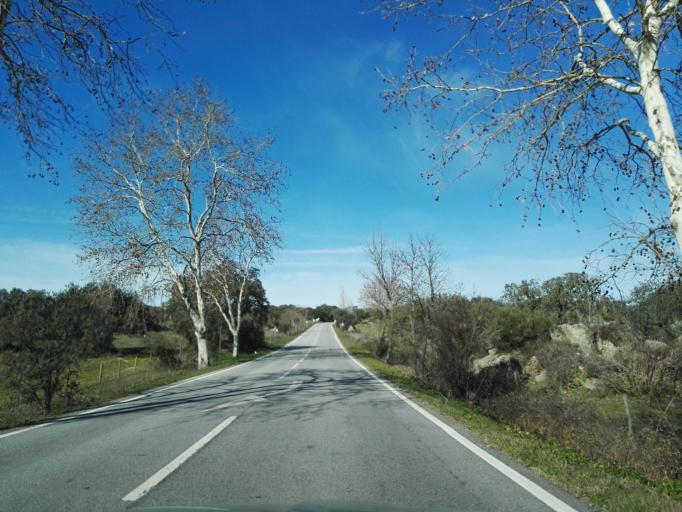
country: PT
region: Portalegre
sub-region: Arronches
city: Arronches
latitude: 39.0568
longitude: -7.2710
